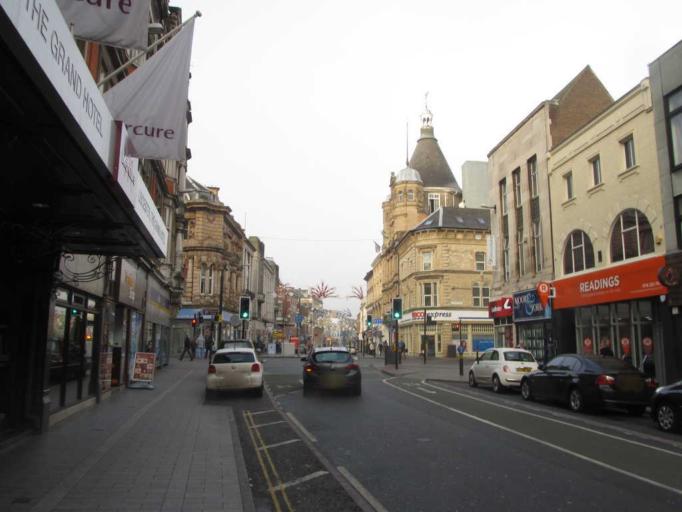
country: GB
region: England
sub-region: City of Leicester
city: Leicester
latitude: 52.6332
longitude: -1.1296
